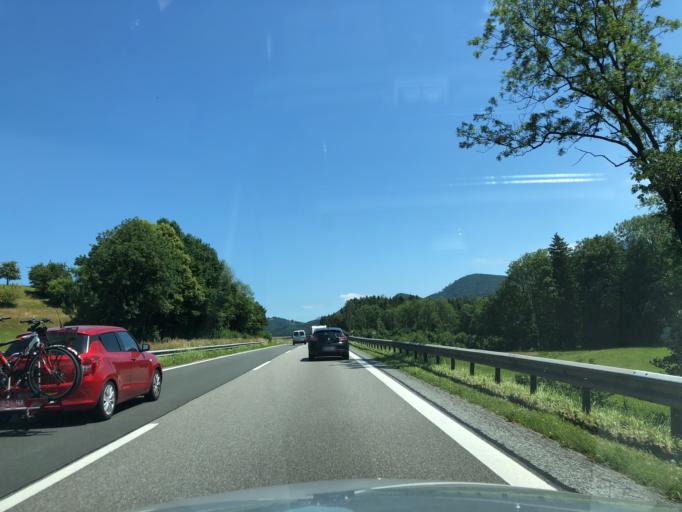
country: DE
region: Bavaria
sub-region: Upper Bavaria
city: Frasdorf
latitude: 47.8023
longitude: 12.3034
